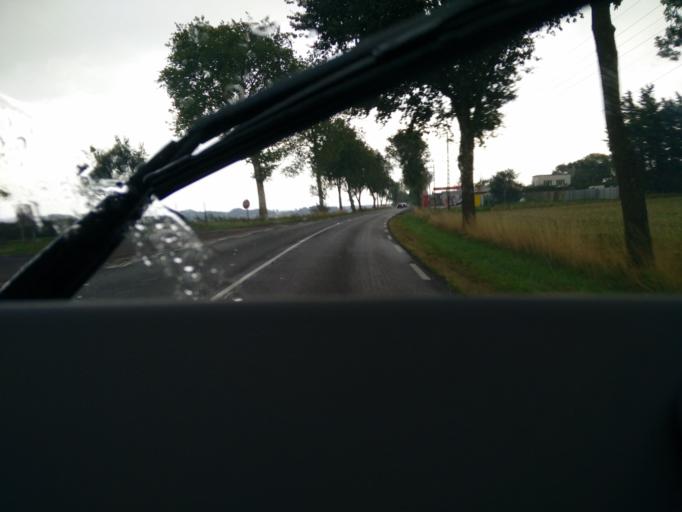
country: FR
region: Nord-Pas-de-Calais
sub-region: Departement du Pas-de-Calais
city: Savy-Berlette
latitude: 50.3489
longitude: 2.5654
